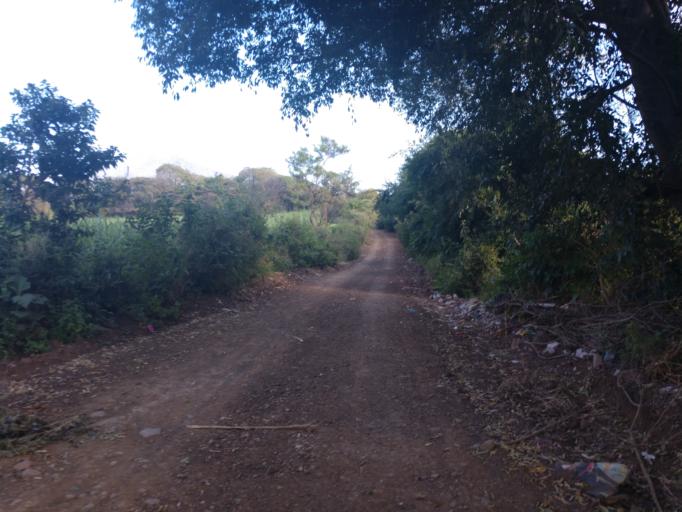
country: MX
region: Nayarit
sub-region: Tepic
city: La Corregidora
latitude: 21.4571
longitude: -104.7973
